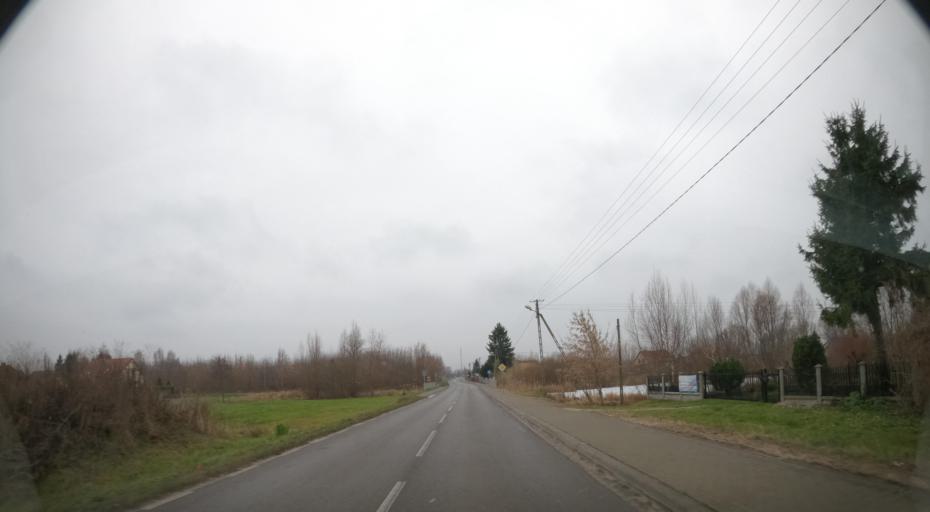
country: PL
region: Masovian Voivodeship
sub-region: Powiat radomski
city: Skaryszew
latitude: 51.3830
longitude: 21.2546
